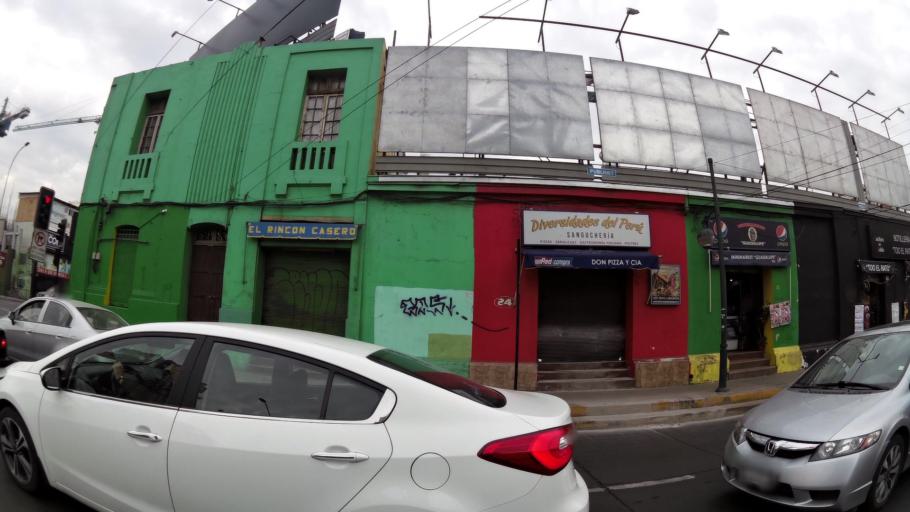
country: CL
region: Santiago Metropolitan
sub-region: Provincia de Santiago
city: Villa Presidente Frei, Nunoa, Santiago, Chile
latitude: -33.4540
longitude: -70.6089
